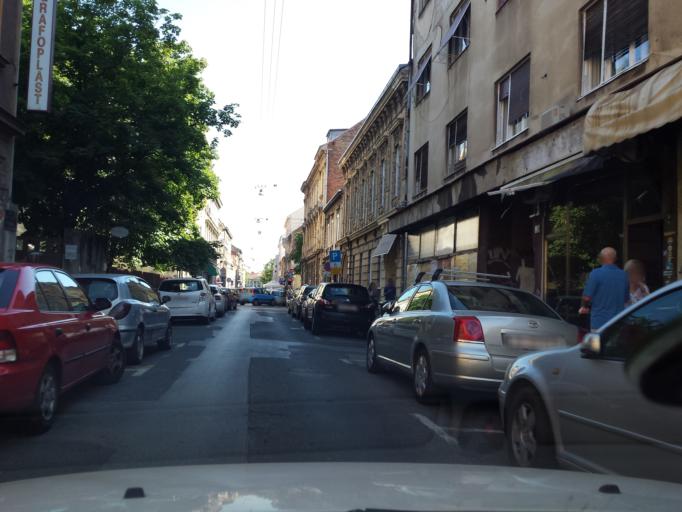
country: HR
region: Grad Zagreb
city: Zagreb - Centar
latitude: 45.8098
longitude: 15.9745
